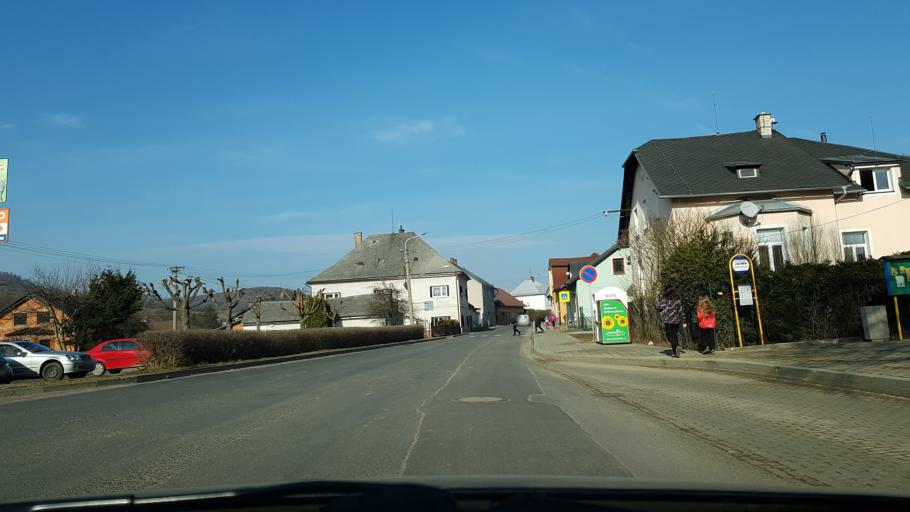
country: CZ
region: Olomoucky
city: Ruda nad Moravou
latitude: 49.9787
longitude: 16.8752
